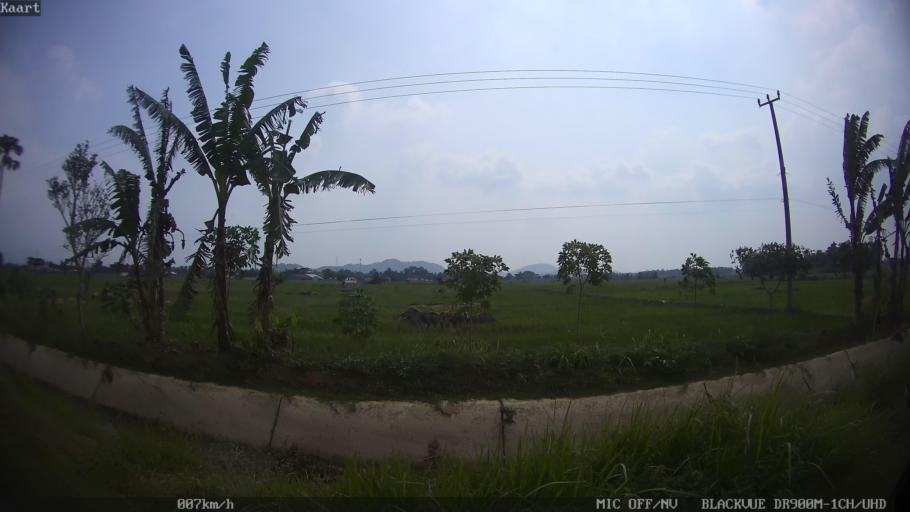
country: ID
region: Lampung
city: Gadingrejo
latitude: -5.3676
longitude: 105.0506
